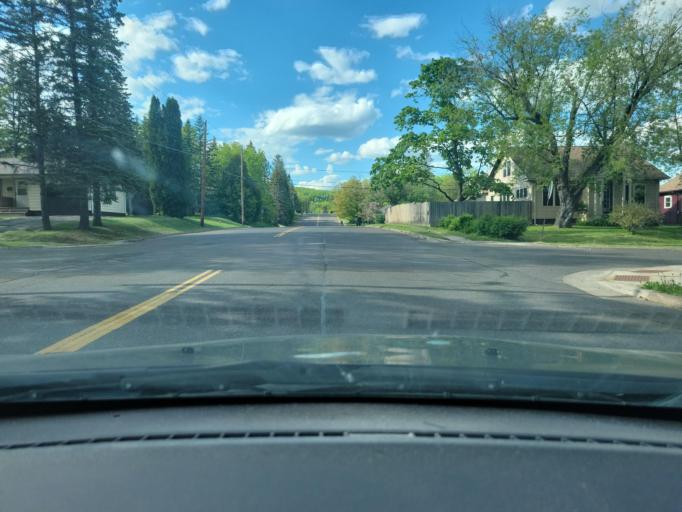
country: US
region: Minnesota
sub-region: Saint Louis County
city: Arnold
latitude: 46.8372
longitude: -92.0293
